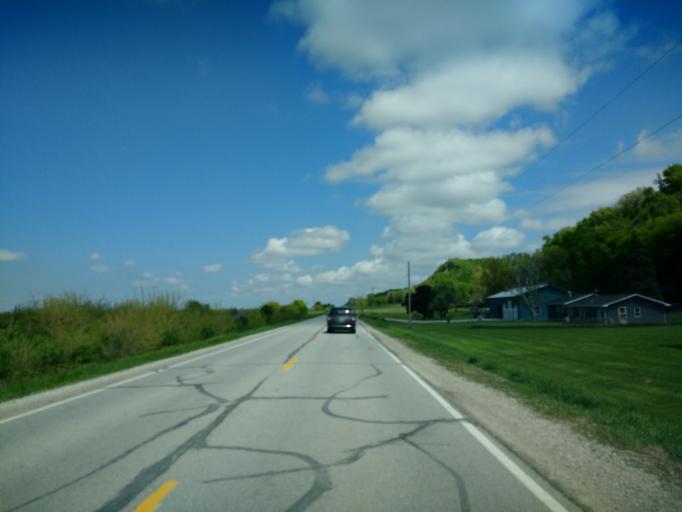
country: US
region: Iowa
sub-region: Harrison County
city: Missouri Valley
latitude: 41.4505
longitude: -95.8727
